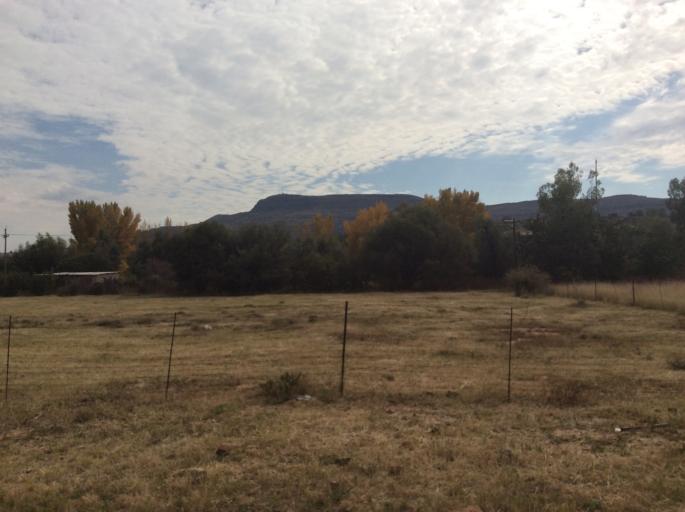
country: LS
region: Mafeteng
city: Mafeteng
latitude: -29.7291
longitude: 27.0290
